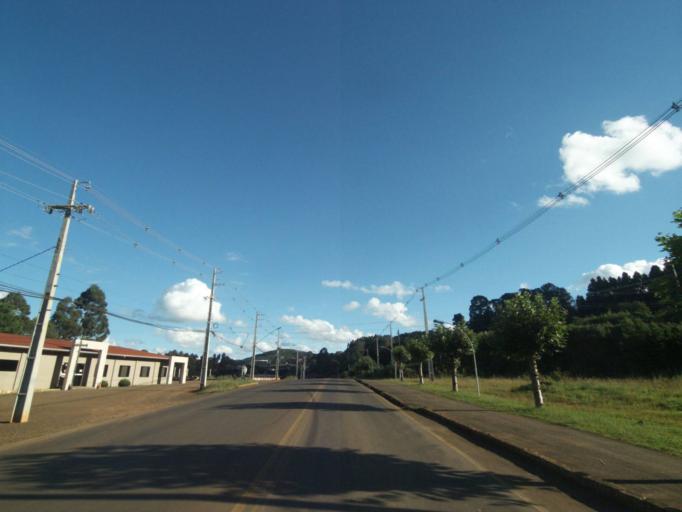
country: BR
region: Parana
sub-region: Uniao Da Vitoria
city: Uniao da Vitoria
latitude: -26.1558
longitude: -51.5422
